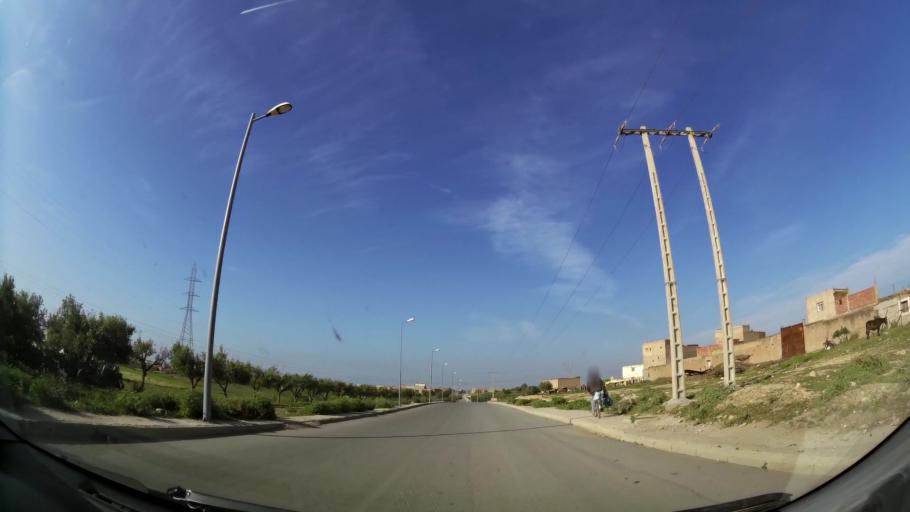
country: MA
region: Oriental
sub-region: Oujda-Angad
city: Oujda
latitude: 34.7168
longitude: -1.9079
